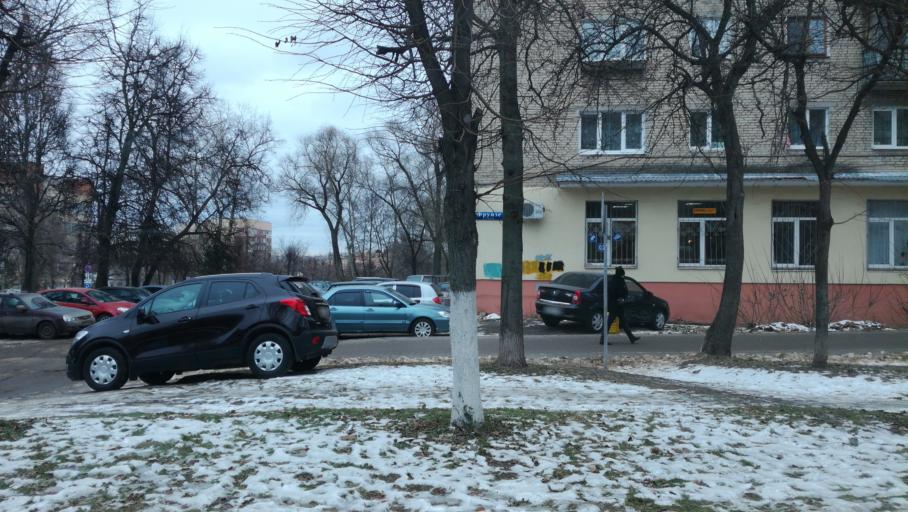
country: RU
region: Tula
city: Tula
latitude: 54.1909
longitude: 37.5921
